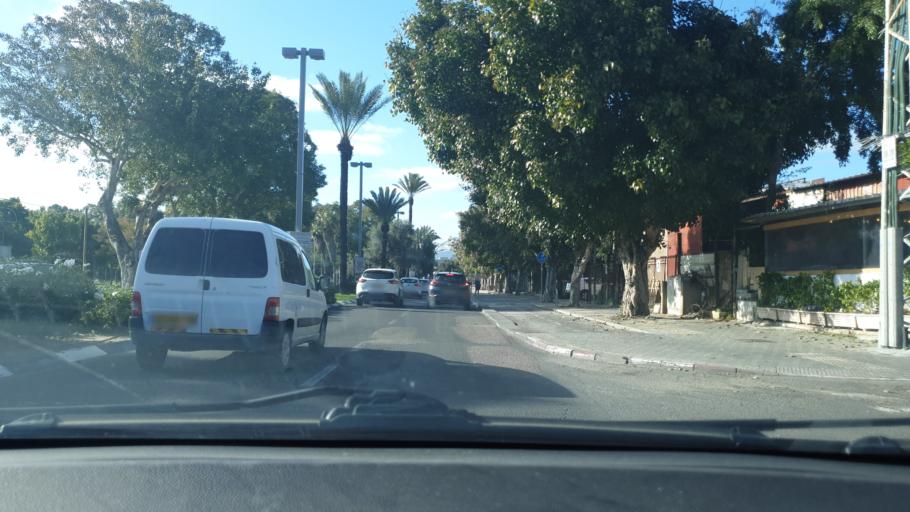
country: IL
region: Tel Aviv
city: Yafo
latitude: 32.0458
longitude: 34.7675
